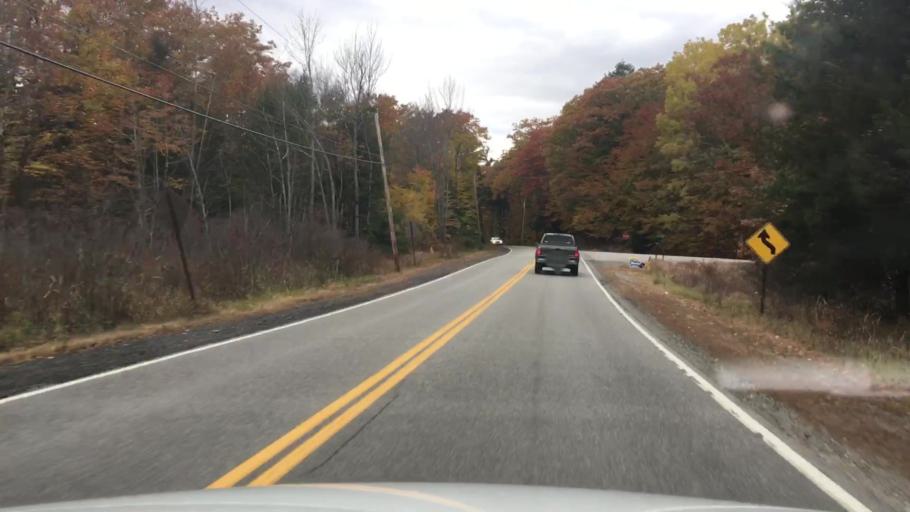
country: US
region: Maine
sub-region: Androscoggin County
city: Sabattus
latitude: 44.1308
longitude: -70.0399
